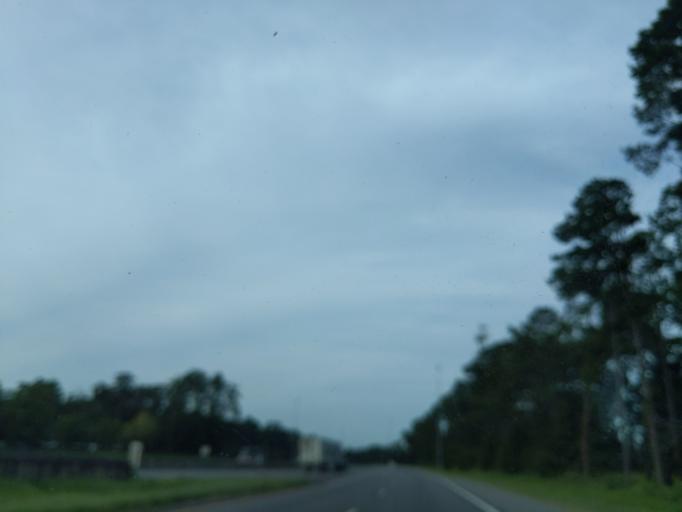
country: US
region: Florida
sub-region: Leon County
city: Tallahassee
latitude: 30.5019
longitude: -84.2559
